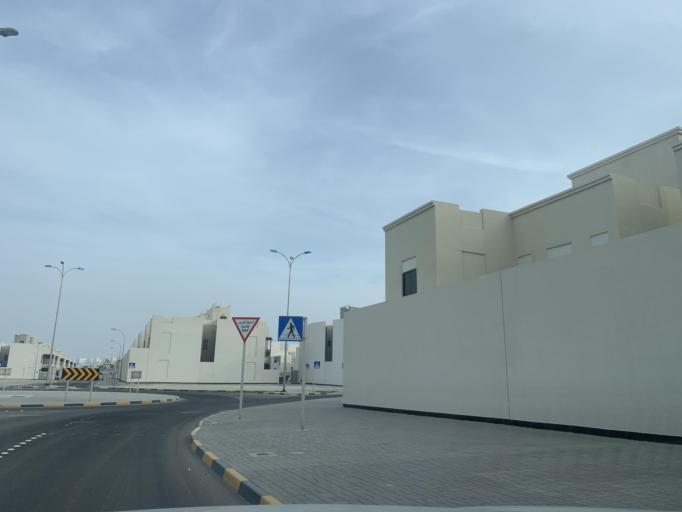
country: BH
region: Muharraq
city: Al Muharraq
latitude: 26.3161
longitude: 50.6241
